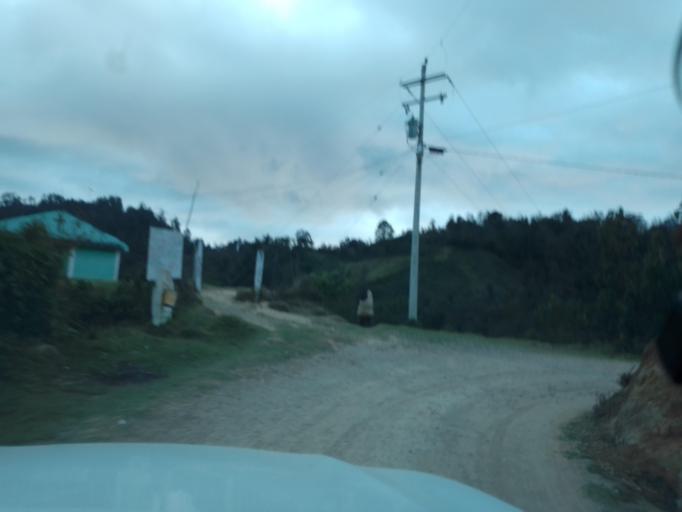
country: MX
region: Chiapas
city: Motozintla de Mendoza
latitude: 15.2160
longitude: -92.2327
